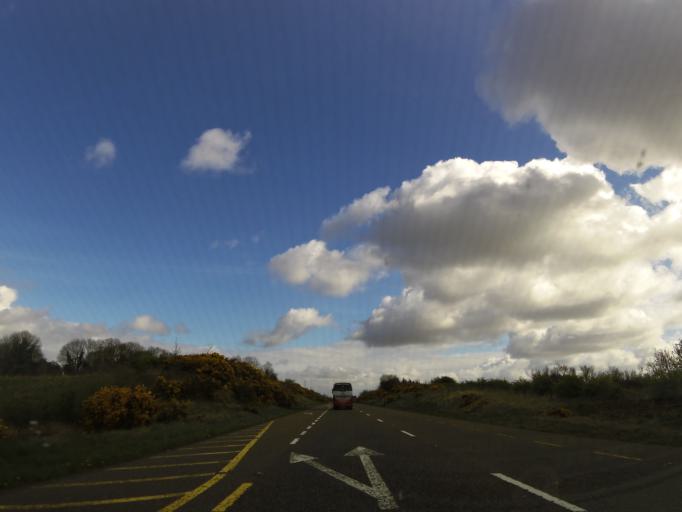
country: IE
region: Connaught
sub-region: Maigh Eo
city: Kiltamagh
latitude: 53.8138
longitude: -8.8981
